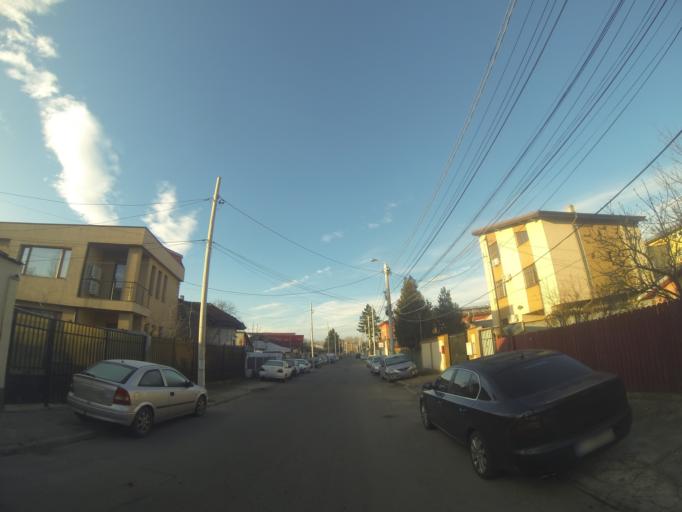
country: RO
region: Bucuresti
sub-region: Municipiul Bucuresti
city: Bucuresti
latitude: 44.4080
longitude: 26.0836
